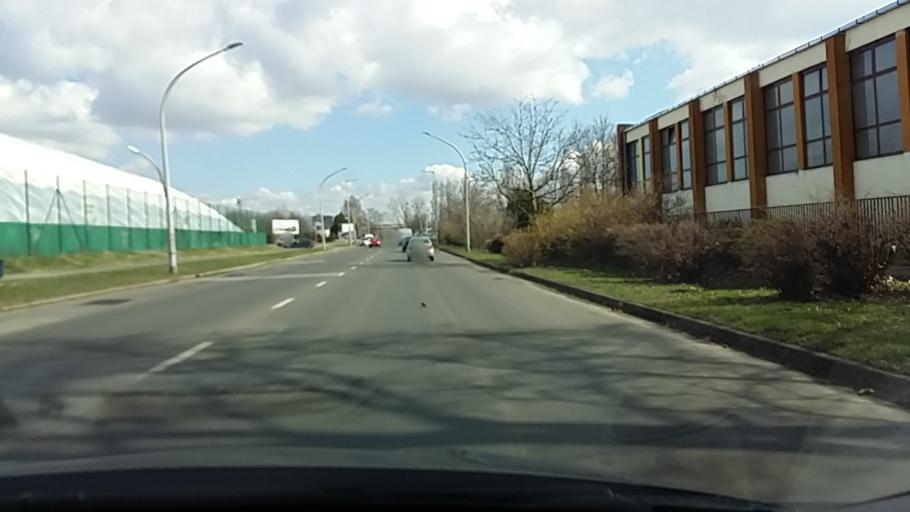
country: HU
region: Baranya
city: Pecs
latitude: 46.0637
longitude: 18.2036
